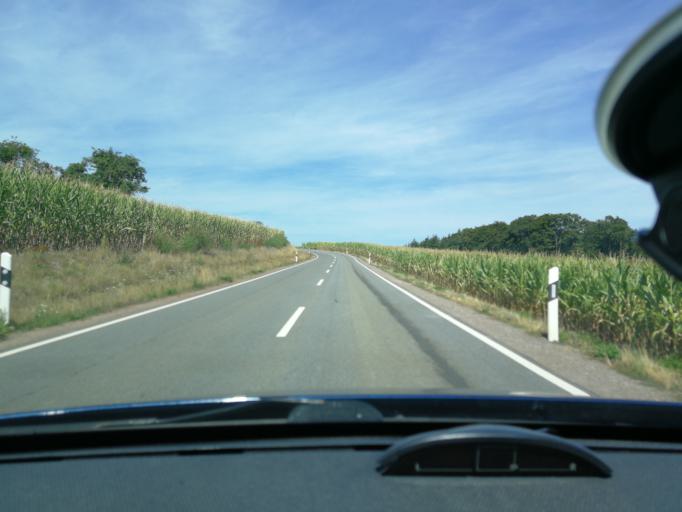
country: DE
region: Rheinland-Pfalz
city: Niersbach
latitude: 49.9282
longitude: 6.7562
